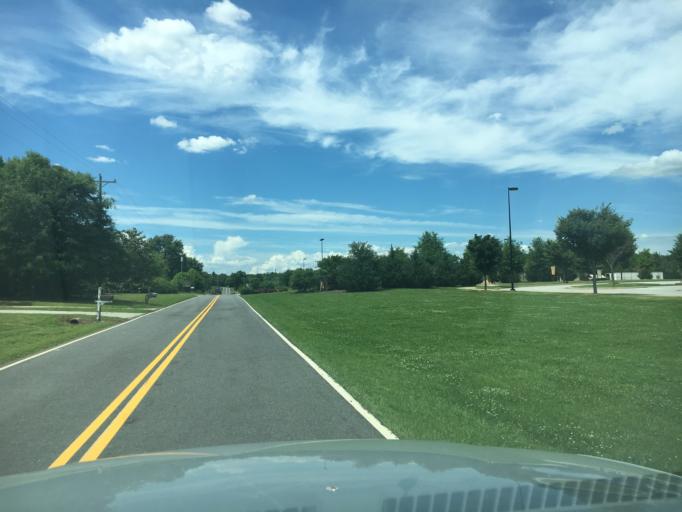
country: US
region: South Carolina
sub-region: Spartanburg County
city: Duncan
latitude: 34.8715
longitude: -82.1077
